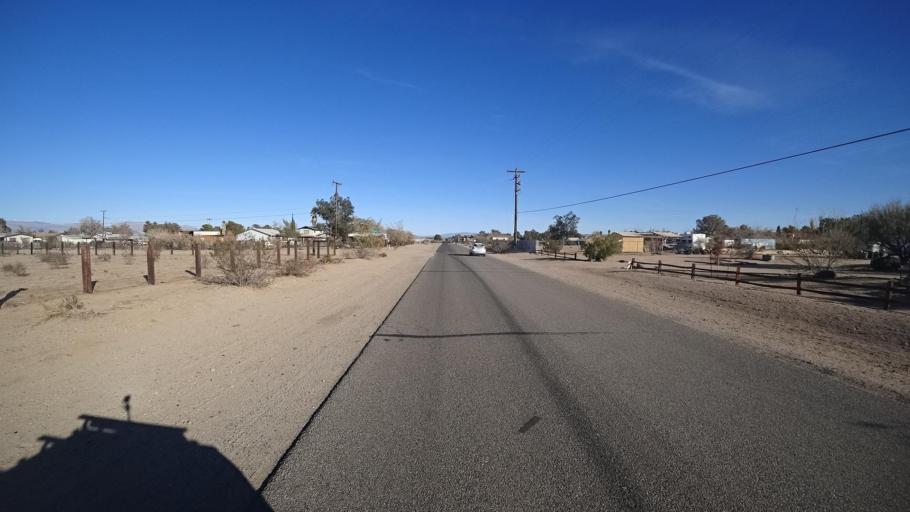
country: US
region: California
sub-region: Kern County
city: Ridgecrest
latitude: 35.6445
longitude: -117.7004
